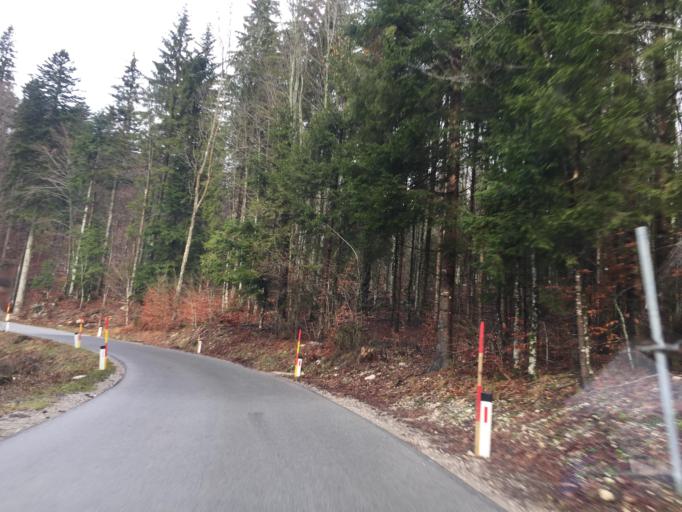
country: SI
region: Ajdovscina
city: Lokavec
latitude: 45.9600
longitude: 13.8546
